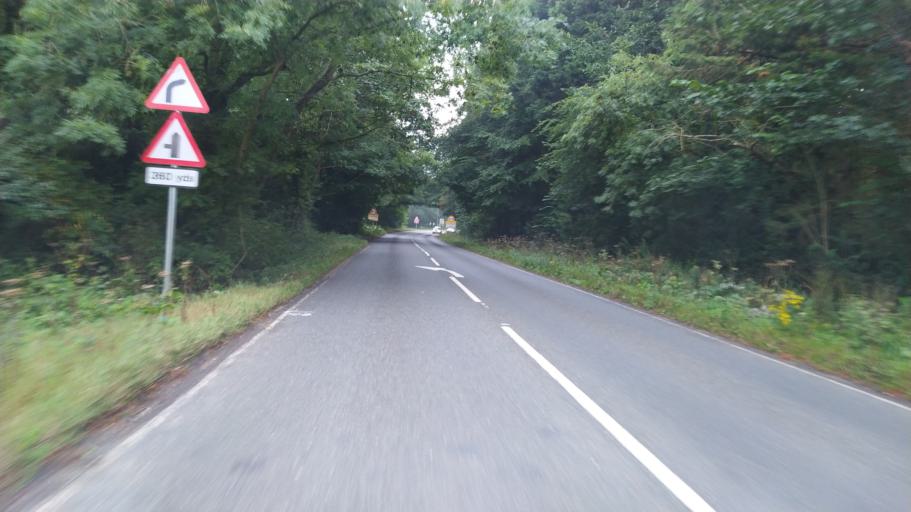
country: GB
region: England
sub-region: Hampshire
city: New Milton
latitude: 50.7651
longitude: -1.6978
